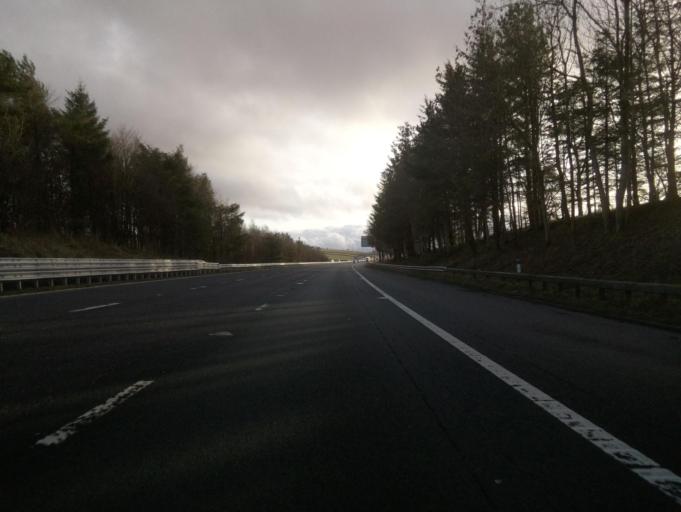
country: GB
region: England
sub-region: Cumbria
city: Penrith
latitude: 54.5327
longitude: -2.6598
